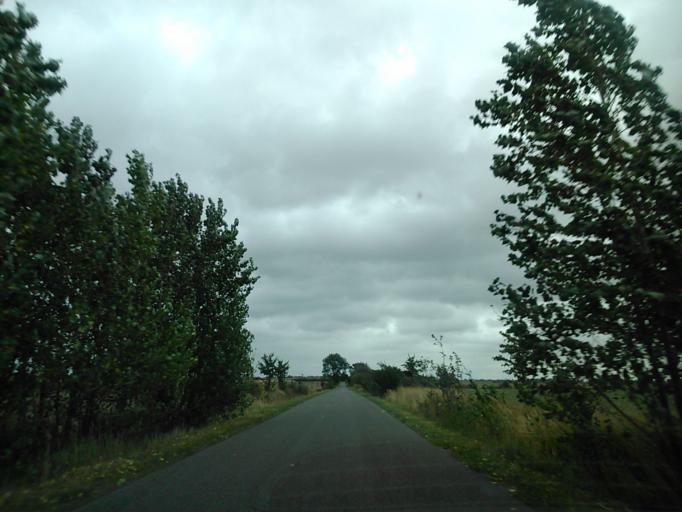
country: PL
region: Greater Poland Voivodeship
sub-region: Powiat koninski
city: Skulsk
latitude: 52.5591
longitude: 18.3907
